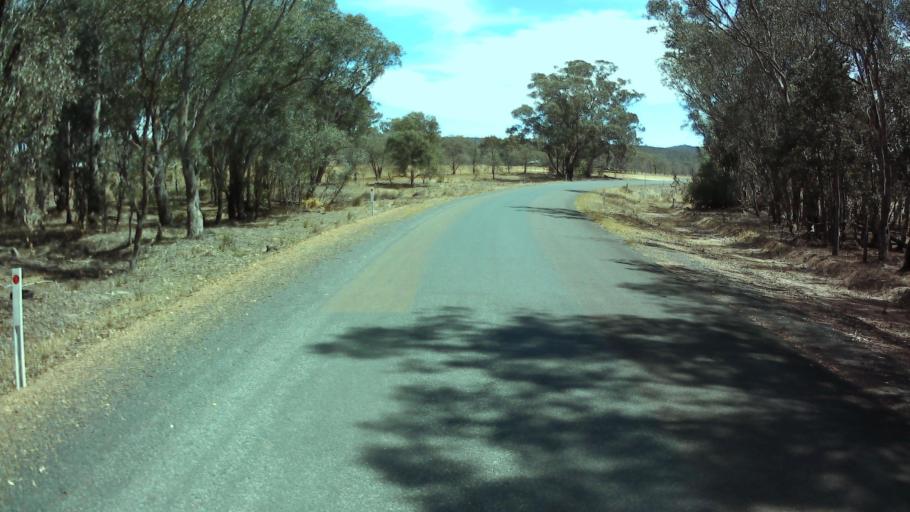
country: AU
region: New South Wales
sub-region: Weddin
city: Grenfell
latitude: -33.7767
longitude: 148.2081
